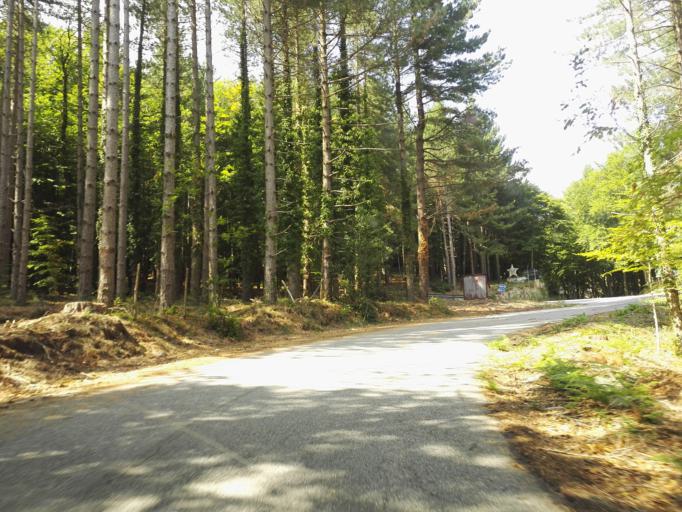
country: IT
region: Calabria
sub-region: Provincia di Vibo-Valentia
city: Nardodipace
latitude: 38.4877
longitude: 16.3774
